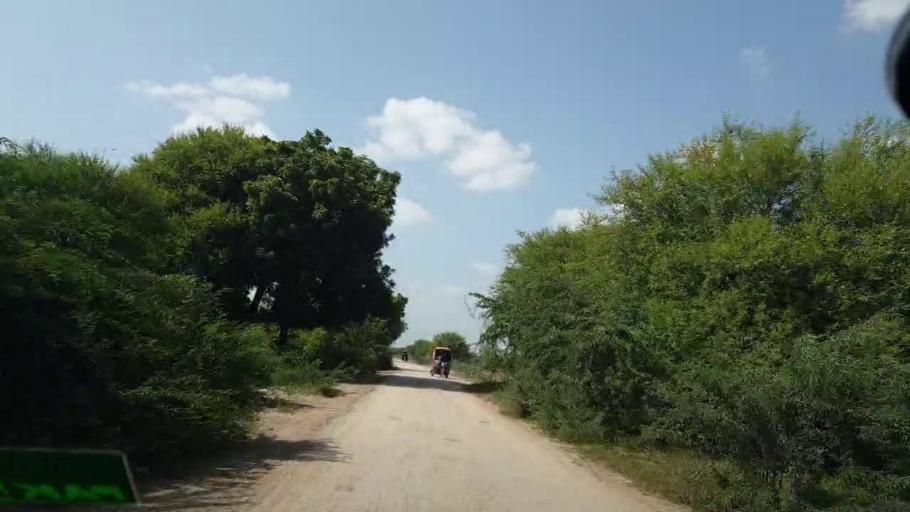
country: PK
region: Sindh
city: Naukot
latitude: 24.6444
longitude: 69.2243
